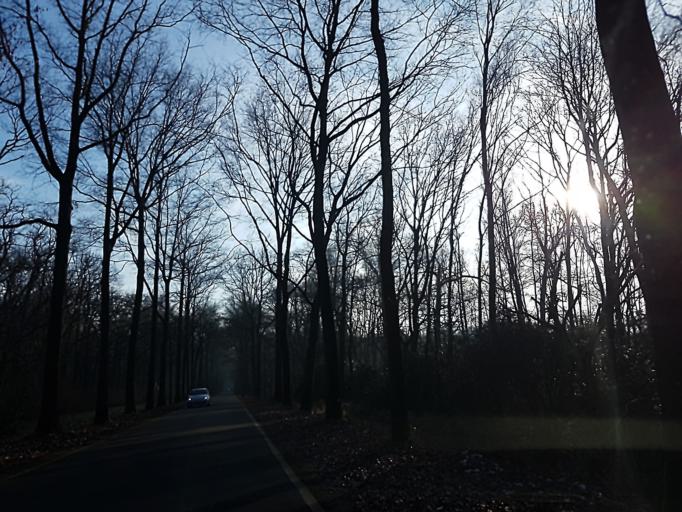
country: BE
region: Flanders
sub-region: Provincie Antwerpen
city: Brasschaat
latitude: 51.3120
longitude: 4.5319
